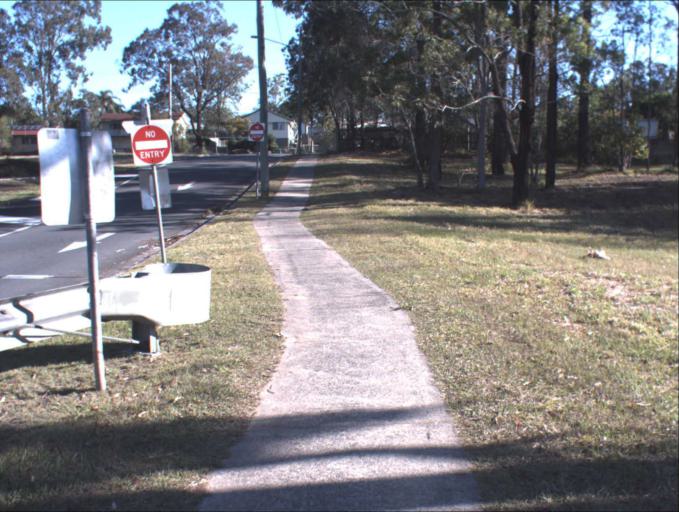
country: AU
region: Queensland
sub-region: Logan
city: Slacks Creek
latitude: -27.6417
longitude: 153.1318
